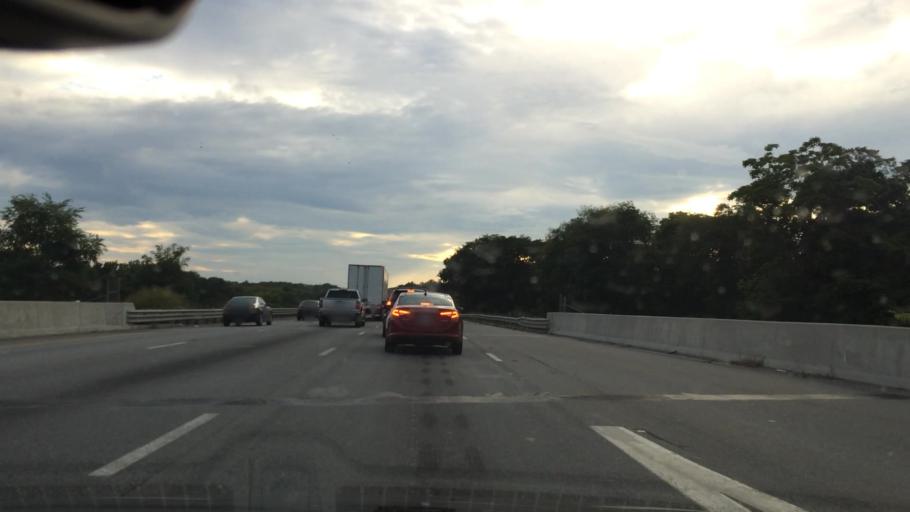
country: US
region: Massachusetts
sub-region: Middlesex County
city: Lowell
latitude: 42.6176
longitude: -71.2920
